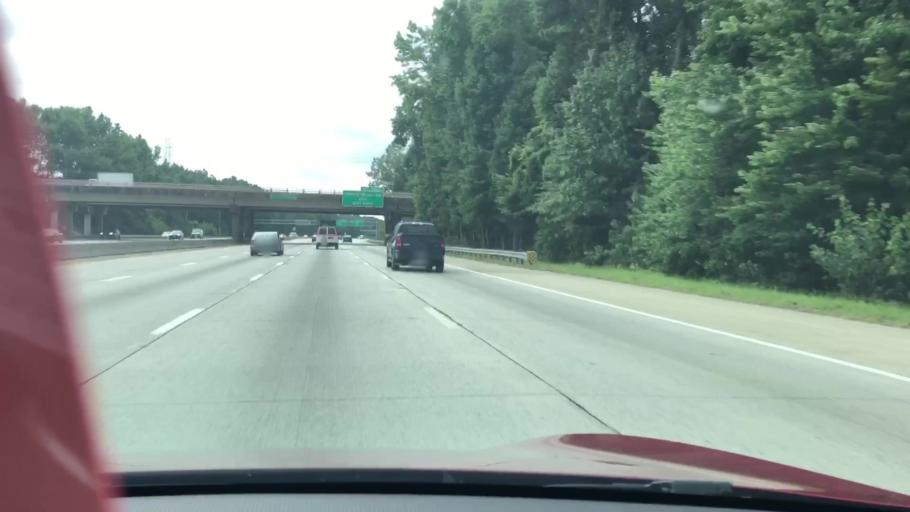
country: US
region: Virginia
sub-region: City of Chesapeake
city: Chesapeake
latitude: 36.8138
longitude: -76.1936
